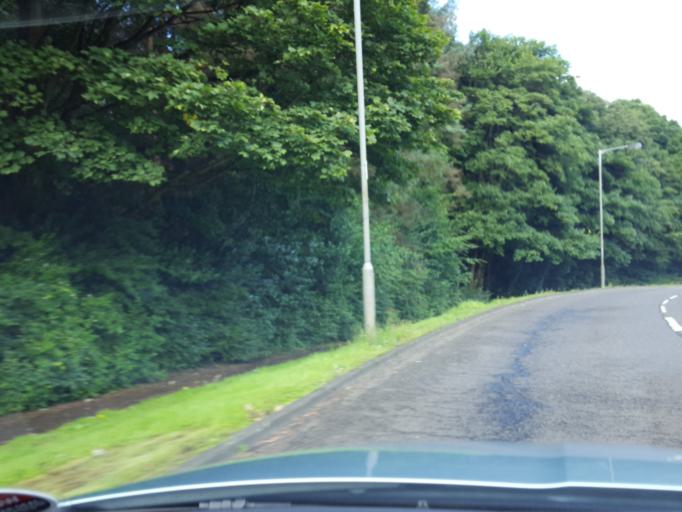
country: GB
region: Scotland
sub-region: Falkirk
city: Bo'ness
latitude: 56.0045
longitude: -3.6303
